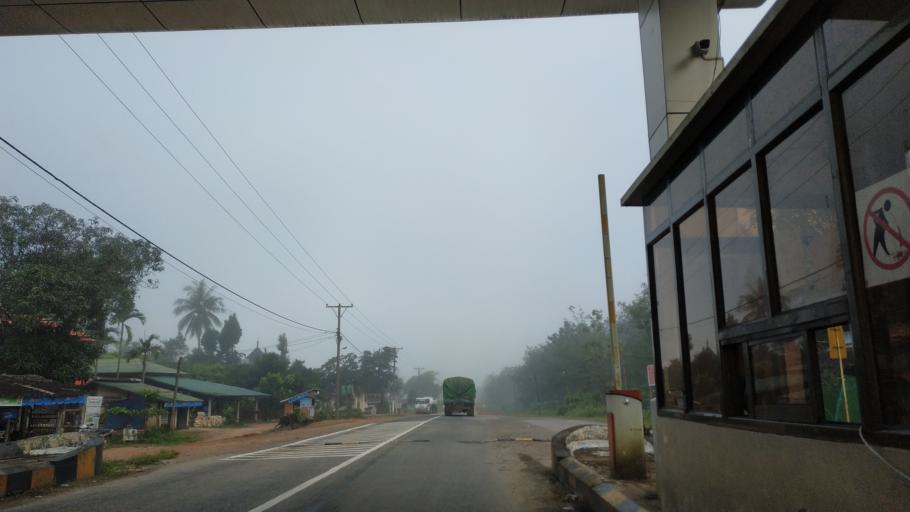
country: MM
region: Tanintharyi
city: Dawei
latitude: 14.1866
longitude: 98.2064
